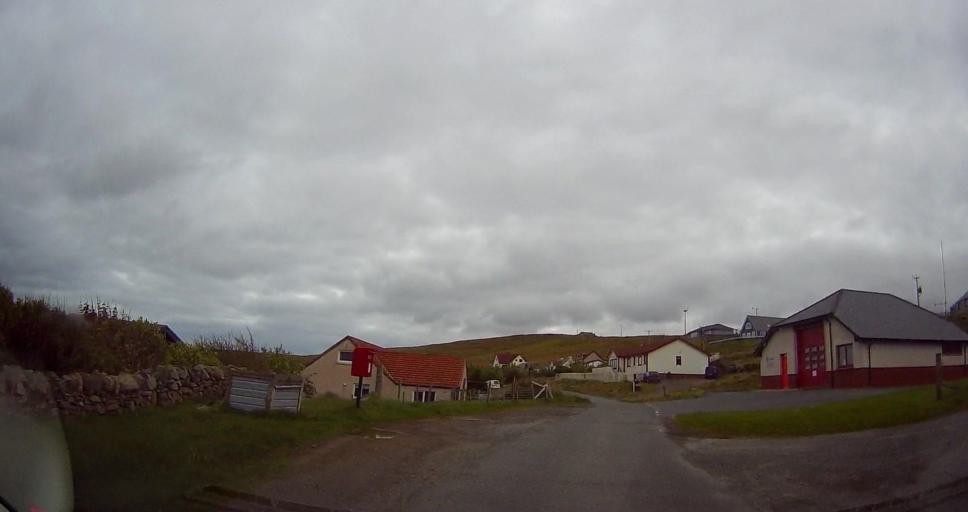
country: GB
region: Scotland
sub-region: Shetland Islands
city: Shetland
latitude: 60.5977
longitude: -1.0746
